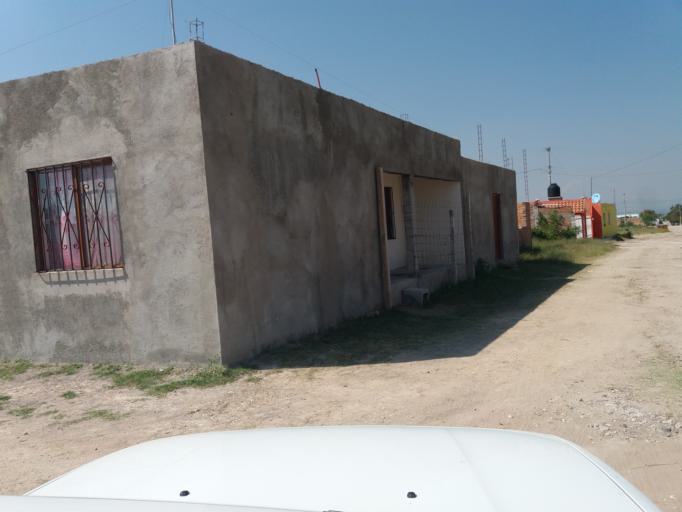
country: MX
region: Aguascalientes
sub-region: Aguascalientes
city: Penuelas (El Cienegal)
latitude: 21.7528
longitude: -102.2628
